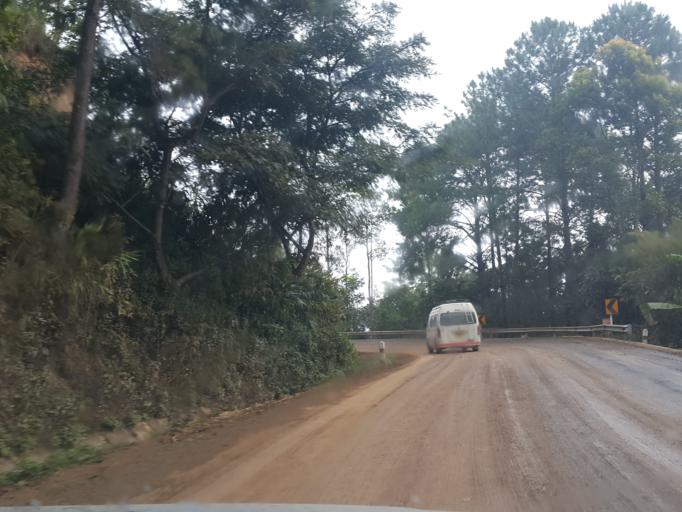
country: TH
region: Mae Hong Son
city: Mae Hi
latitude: 19.2672
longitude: 98.5825
